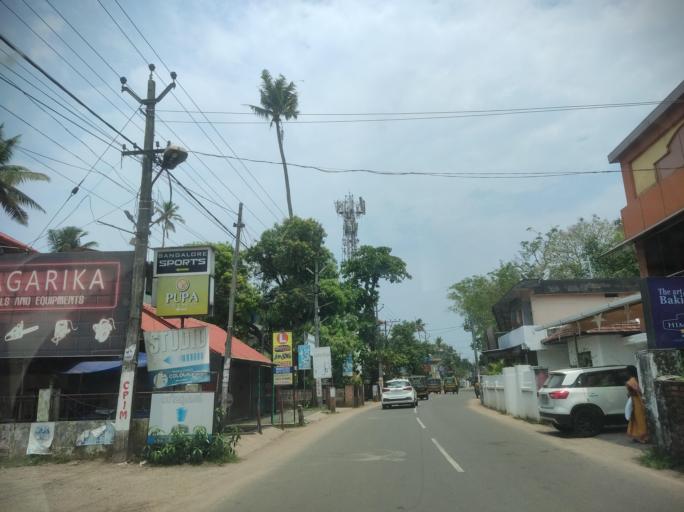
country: IN
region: Kerala
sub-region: Alappuzha
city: Shertallai
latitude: 9.6877
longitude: 76.3419
